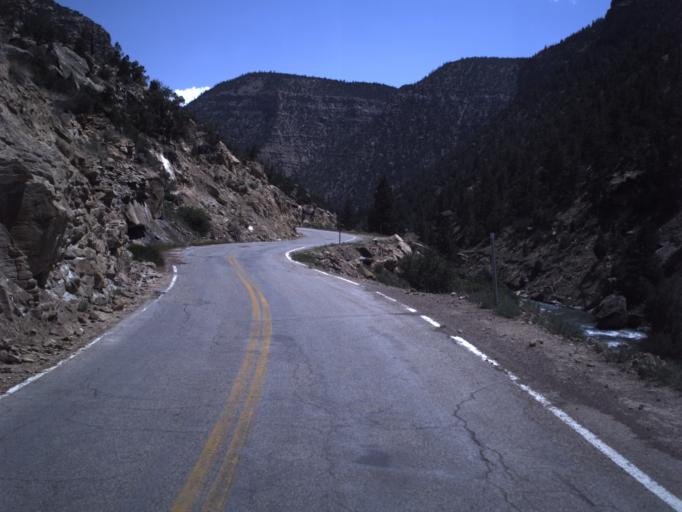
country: US
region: Utah
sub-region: Emery County
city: Orangeville
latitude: 39.2853
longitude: -111.2369
